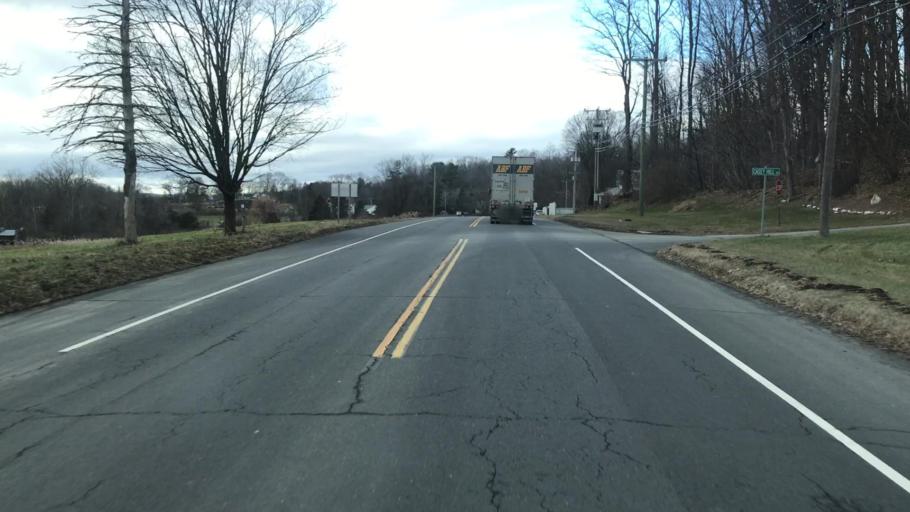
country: US
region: Connecticut
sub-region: Litchfield County
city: Canaan
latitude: 42.0138
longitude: -73.2841
